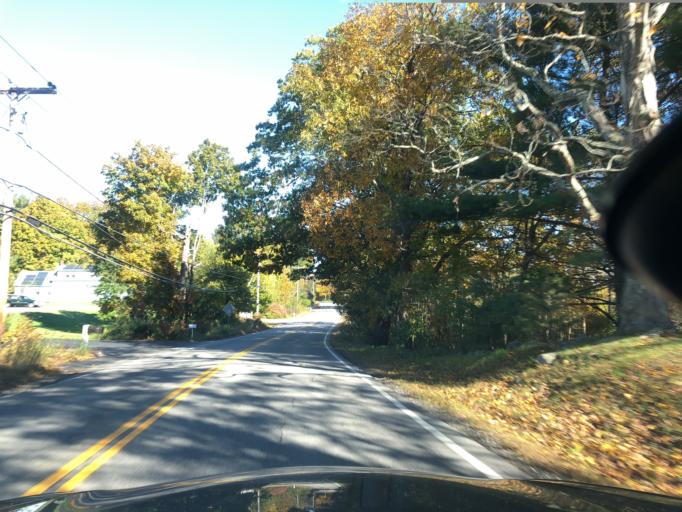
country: US
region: New Hampshire
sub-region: Rockingham County
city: Exeter
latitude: 43.0078
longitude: -70.9456
